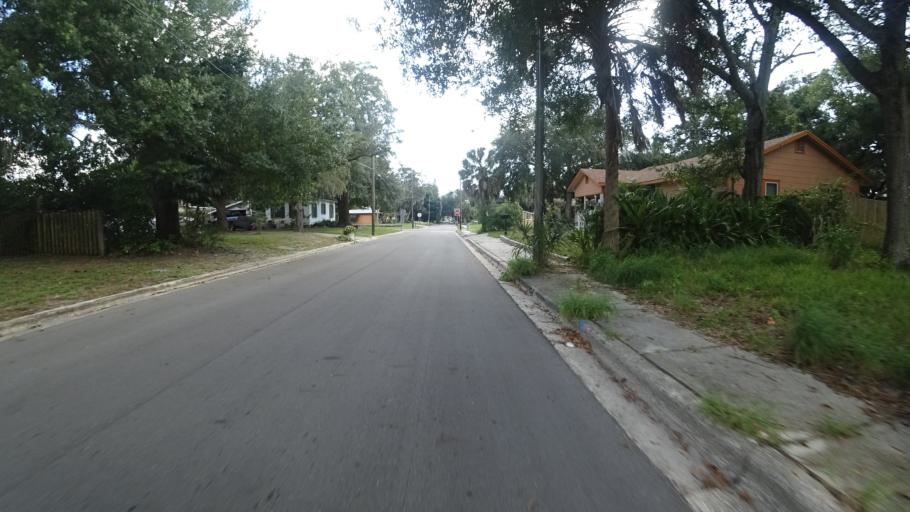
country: US
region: Florida
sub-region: Manatee County
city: Bradenton
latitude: 27.4897
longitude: -82.5803
